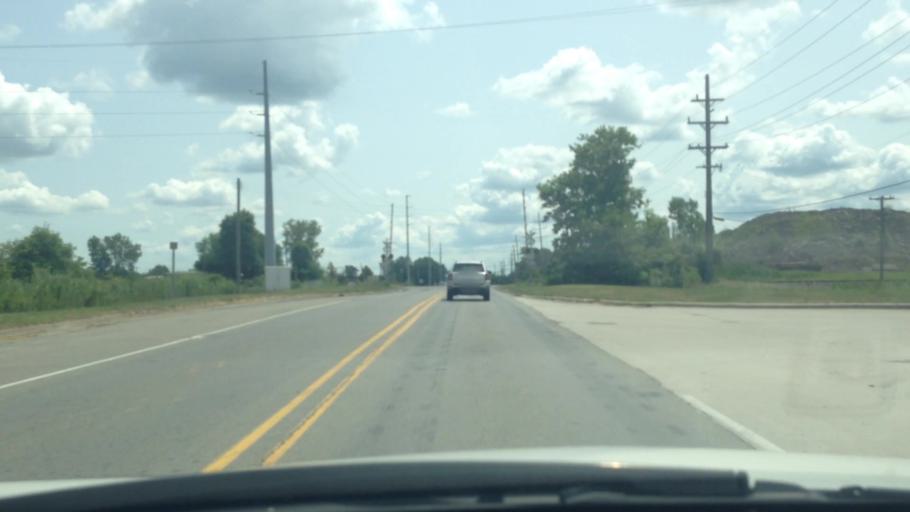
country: US
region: Michigan
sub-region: Wayne County
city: Taylor
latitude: 42.2457
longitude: -83.3083
